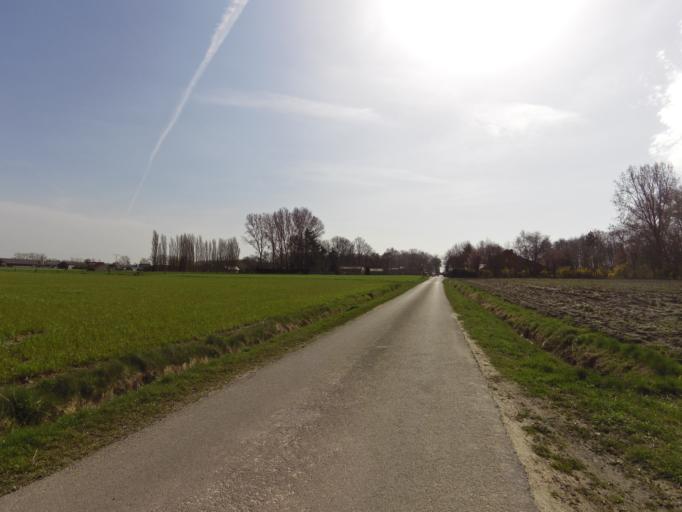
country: BE
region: Flanders
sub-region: Provincie West-Vlaanderen
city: Gistel
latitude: 51.1290
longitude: 2.9665
